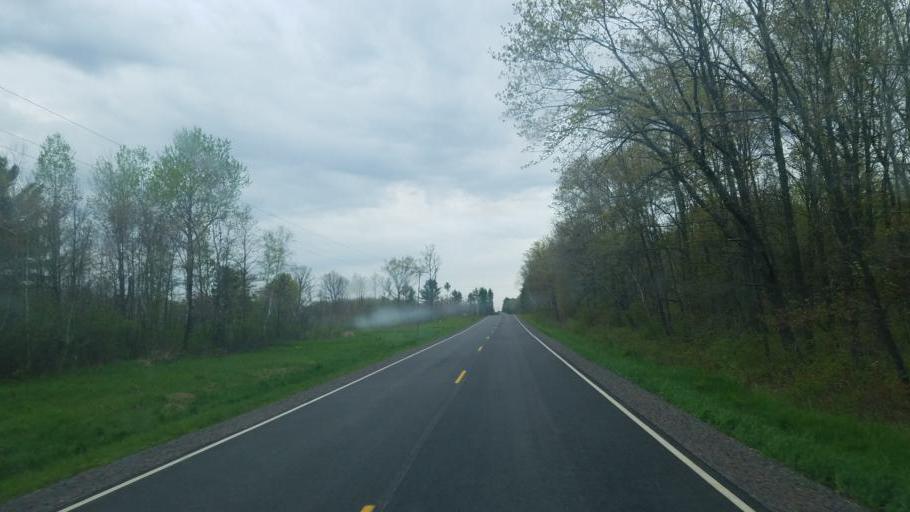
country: US
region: Wisconsin
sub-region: Wood County
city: Marshfield
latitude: 44.4910
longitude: -90.2796
